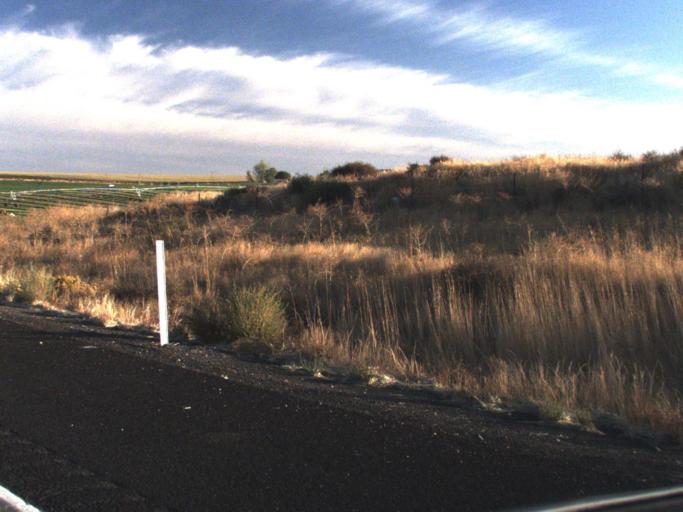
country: US
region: Washington
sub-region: Franklin County
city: Pasco
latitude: 46.2765
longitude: -119.0905
